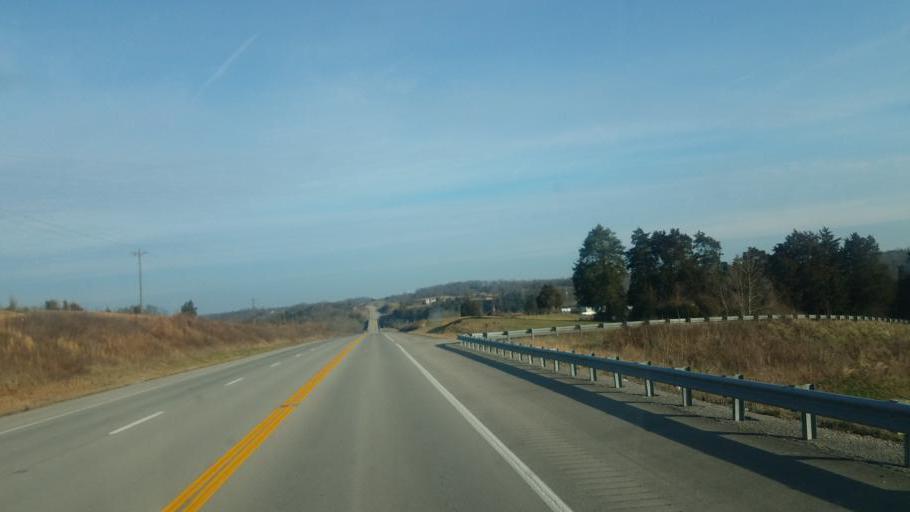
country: US
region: Kentucky
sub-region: Russell County
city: Jamestown
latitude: 36.9594
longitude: -85.0894
